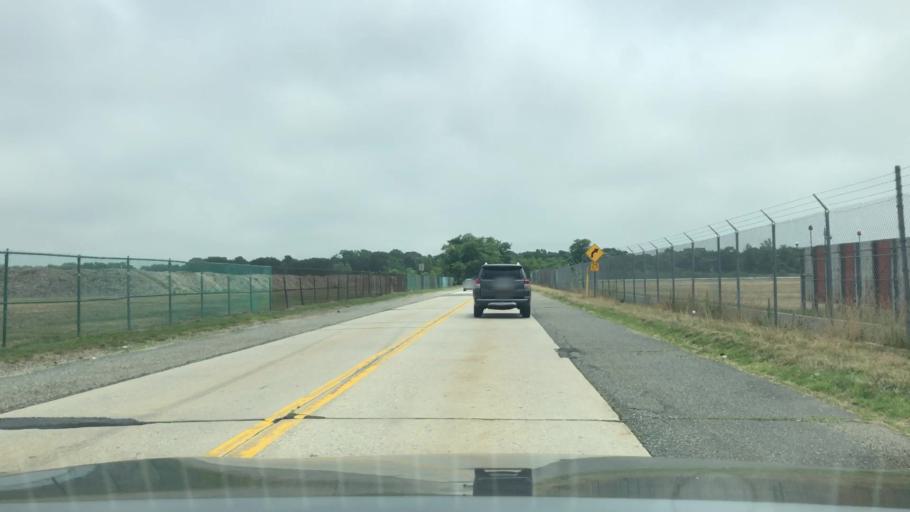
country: US
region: New York
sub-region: Suffolk County
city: East Farmingdale
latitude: 40.7233
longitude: -73.4026
